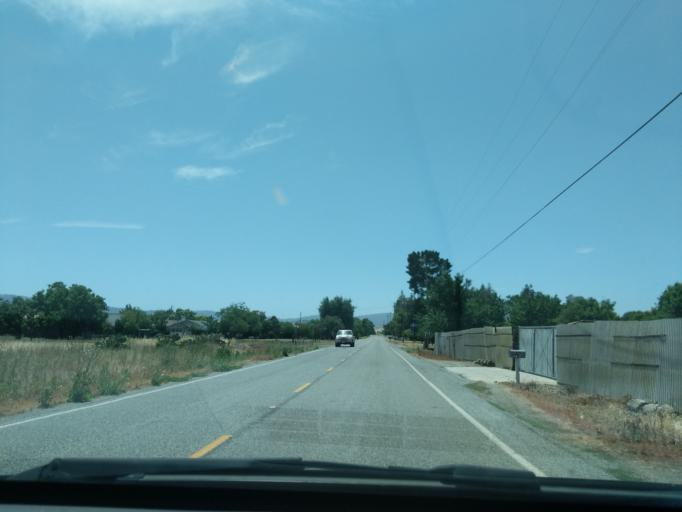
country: US
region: California
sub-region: Santa Clara County
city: San Martin
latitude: 37.0555
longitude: -121.5761
